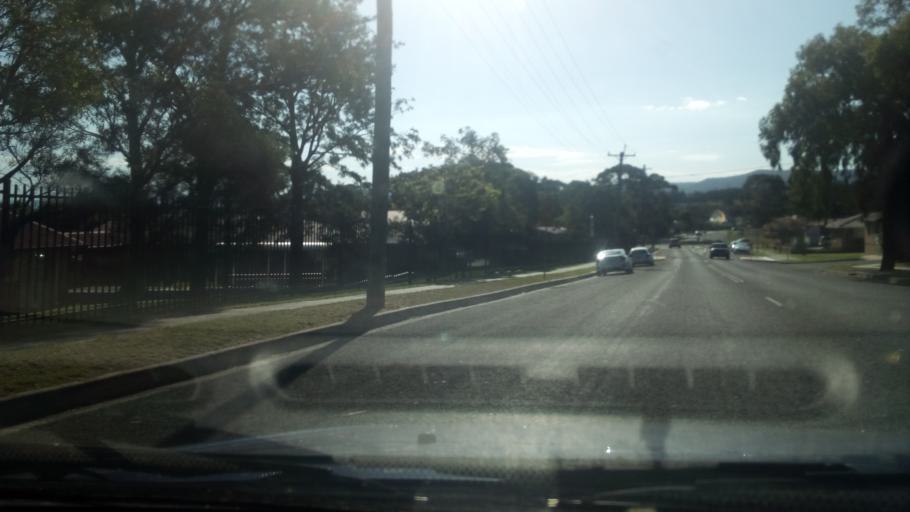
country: AU
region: New South Wales
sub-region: Wollongong
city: Berkeley
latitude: -34.4796
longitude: 150.8568
